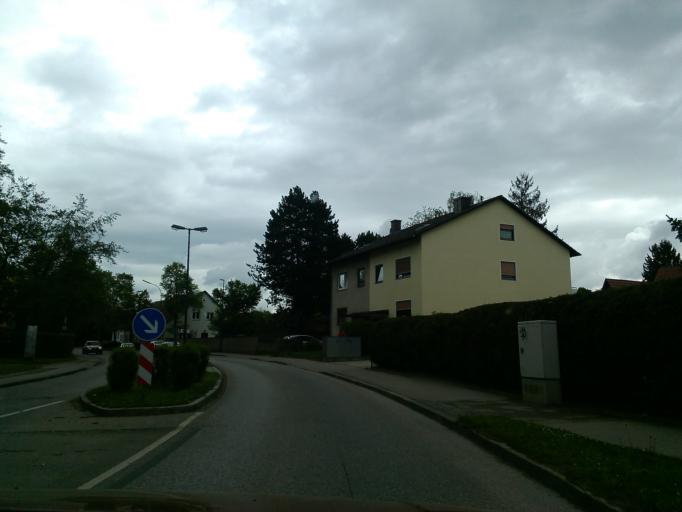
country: DE
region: Bavaria
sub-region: Upper Bavaria
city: Grafelfing
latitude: 48.1139
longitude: 11.4361
